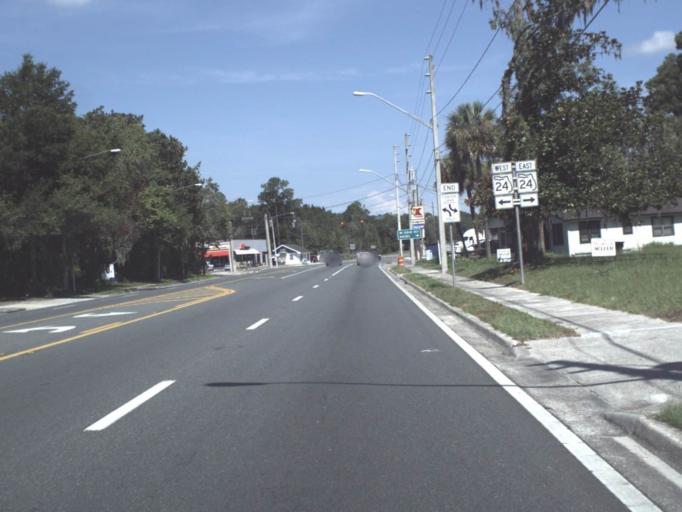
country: US
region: Florida
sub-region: Levy County
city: Bronson
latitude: 29.4471
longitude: -82.6411
